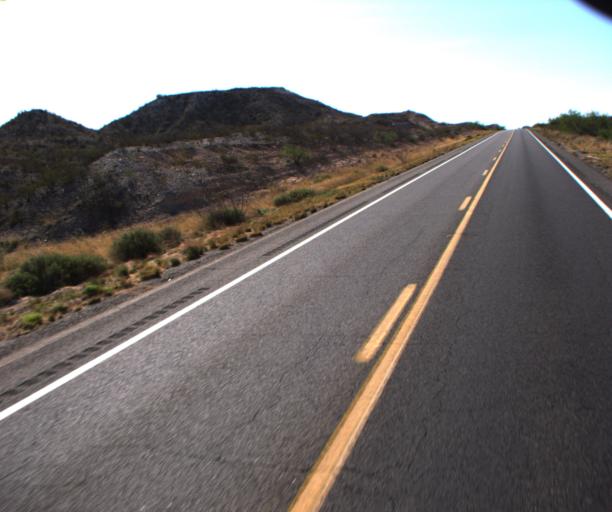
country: US
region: Arizona
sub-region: Cochise County
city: Saint David
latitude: 31.8318
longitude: -110.1820
